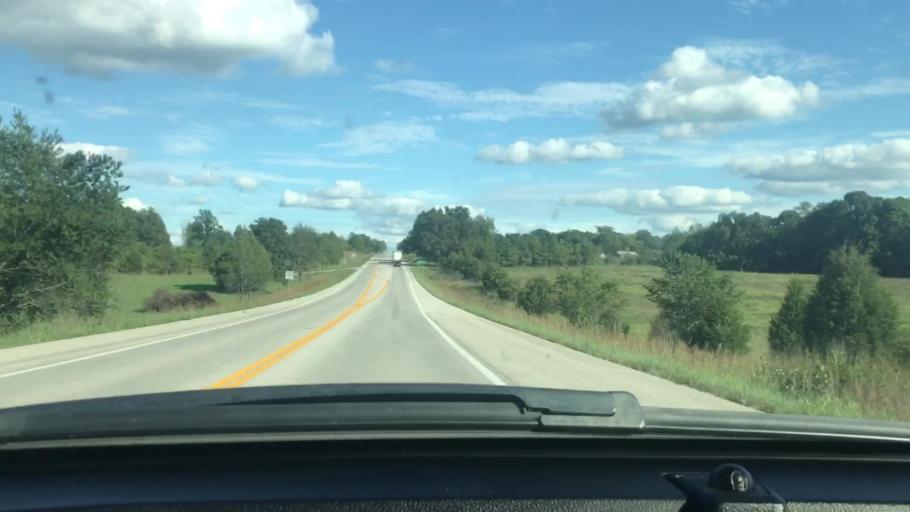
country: US
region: Missouri
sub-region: Howell County
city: West Plains
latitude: 36.6555
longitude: -91.6981
